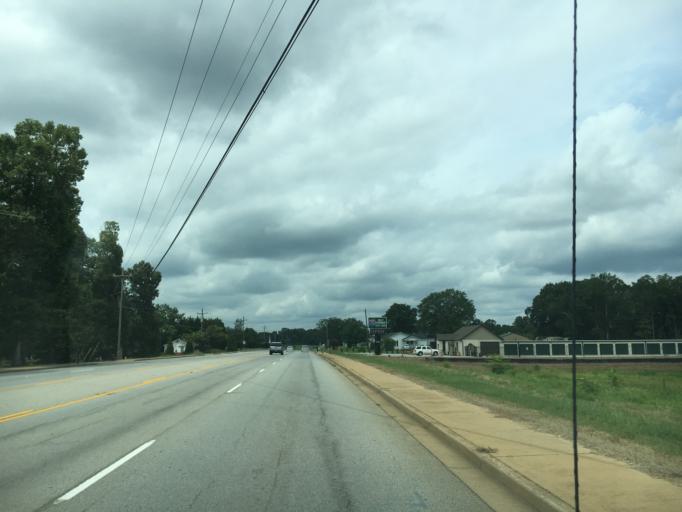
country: US
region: South Carolina
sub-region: Spartanburg County
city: Roebuck
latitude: 34.8792
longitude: -82.0517
